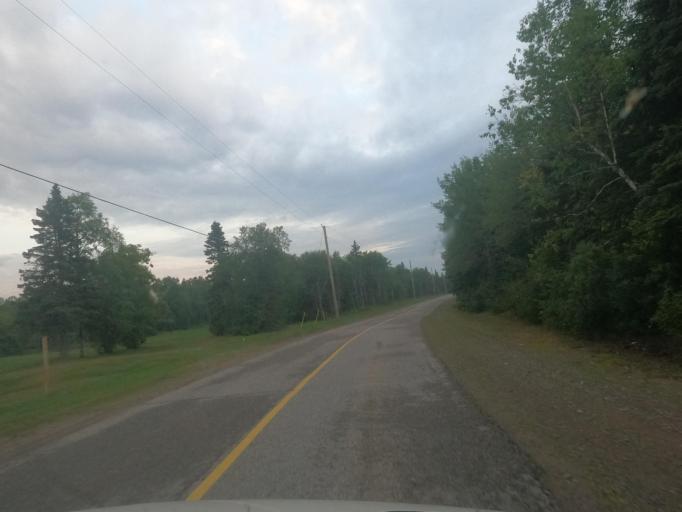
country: CA
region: Ontario
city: Marathon
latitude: 48.7748
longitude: -87.1103
